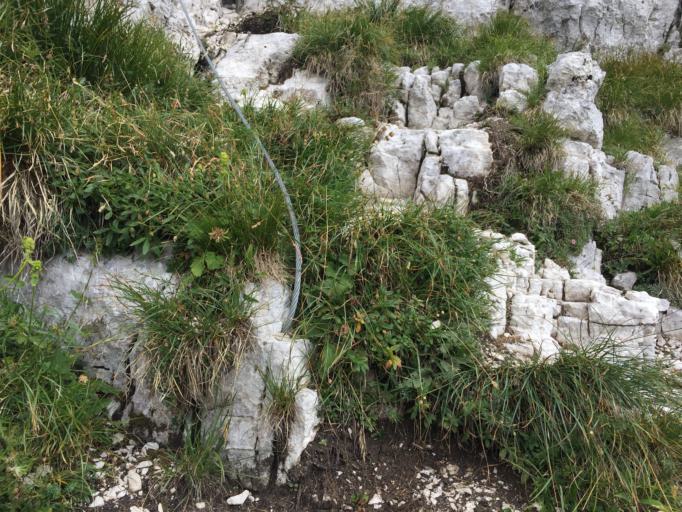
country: IT
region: Veneto
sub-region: Provincia di Belluno
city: Tambre
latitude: 46.1280
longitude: 12.4996
